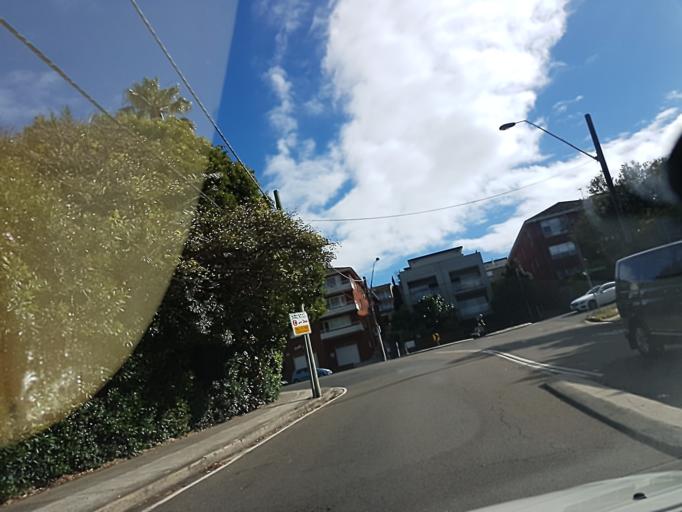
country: AU
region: New South Wales
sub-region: Warringah
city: Freshwater
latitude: -33.7836
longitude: 151.2854
